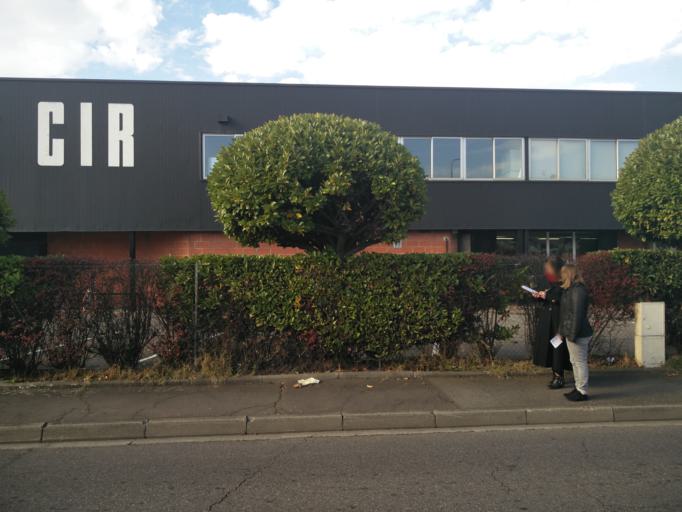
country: FR
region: Midi-Pyrenees
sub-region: Departement de la Haute-Garonne
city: Toulouse
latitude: 43.5718
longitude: 1.4104
